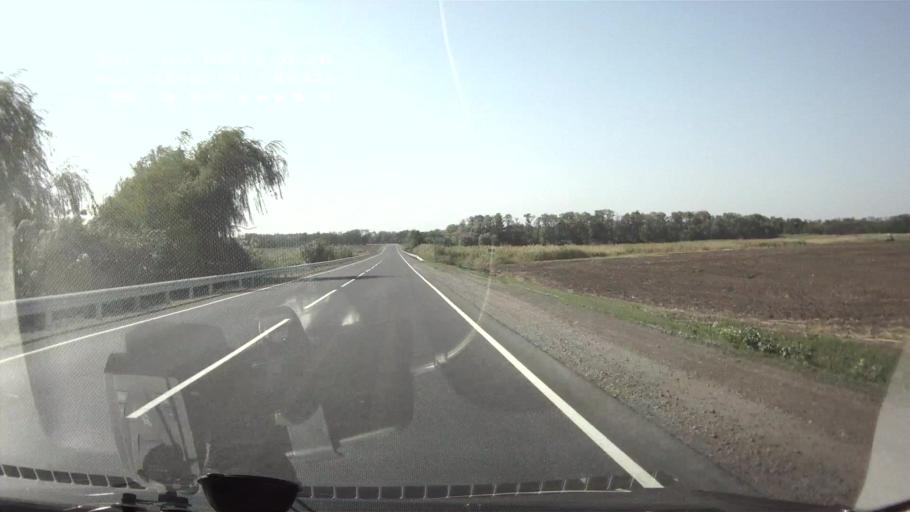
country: RU
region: Krasnodarskiy
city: Kavkazskaya
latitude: 45.5462
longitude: 40.6876
